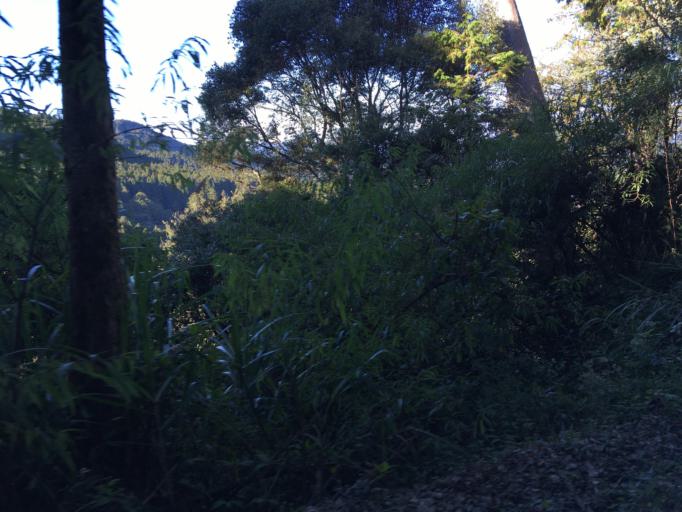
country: TW
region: Taiwan
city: Lugu
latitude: 23.5170
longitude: 120.8069
